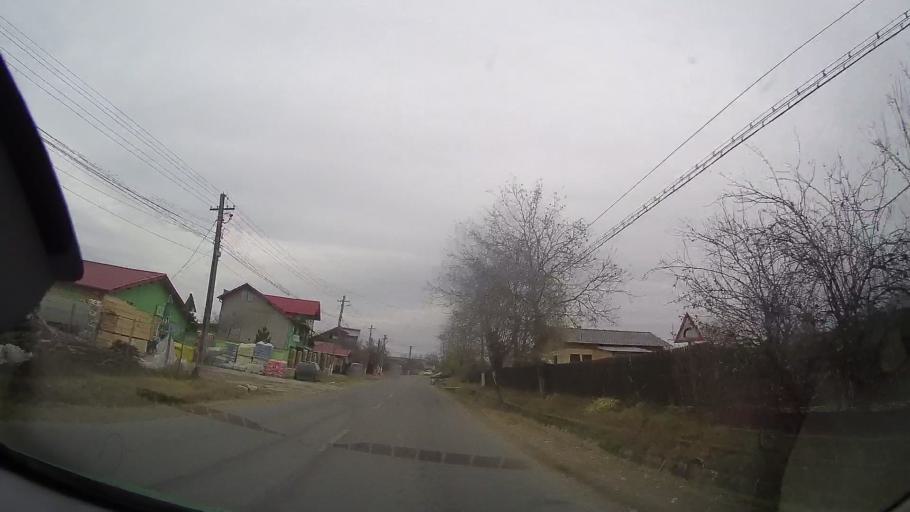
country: RO
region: Prahova
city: Mocesti
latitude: 45.0594
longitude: 26.2433
